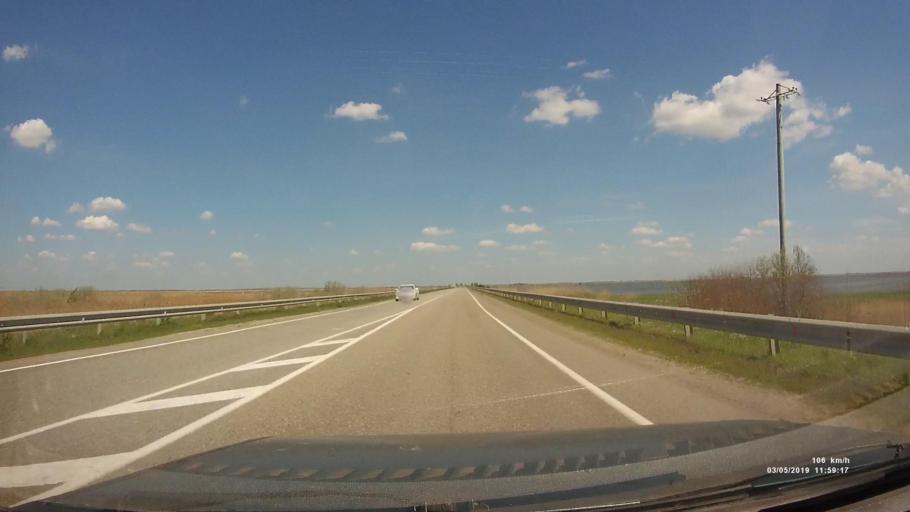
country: RU
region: Rostov
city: Bagayevskaya
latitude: 47.2329
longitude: 40.3289
